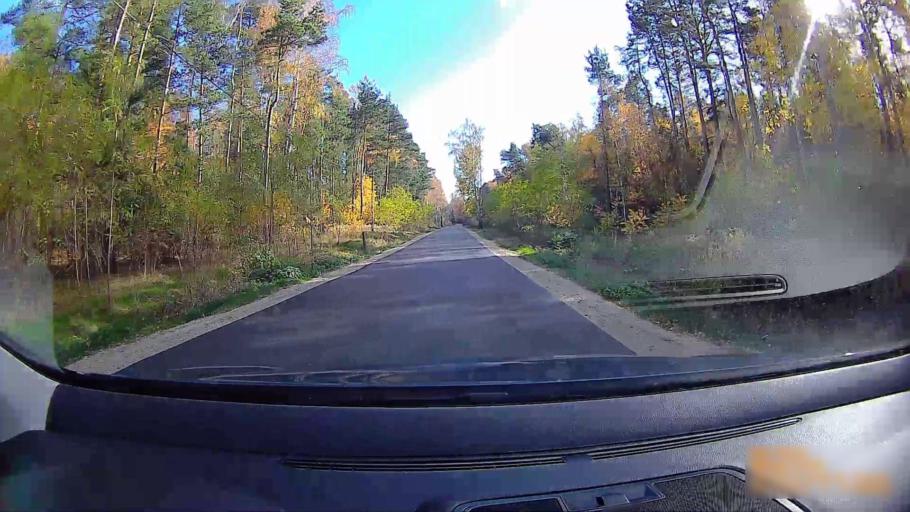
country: PL
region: Greater Poland Voivodeship
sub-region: Powiat ostrzeszowski
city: Ostrzeszow
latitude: 51.4090
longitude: 17.9974
